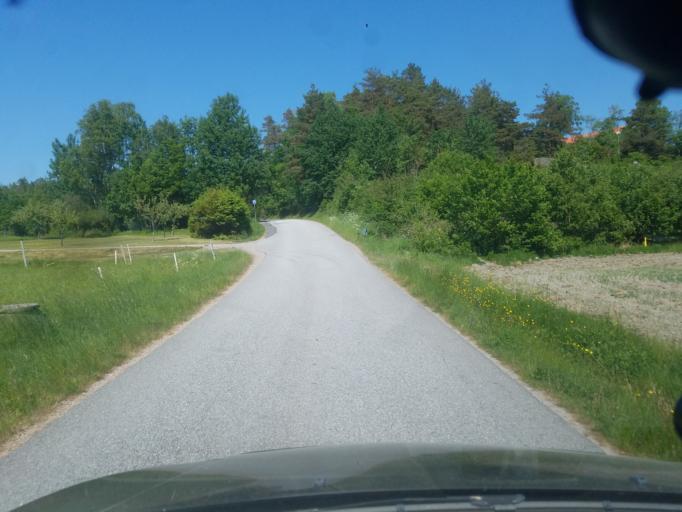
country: SE
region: Vaestra Goetaland
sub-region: Orust
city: Henan
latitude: 58.2839
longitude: 11.5794
